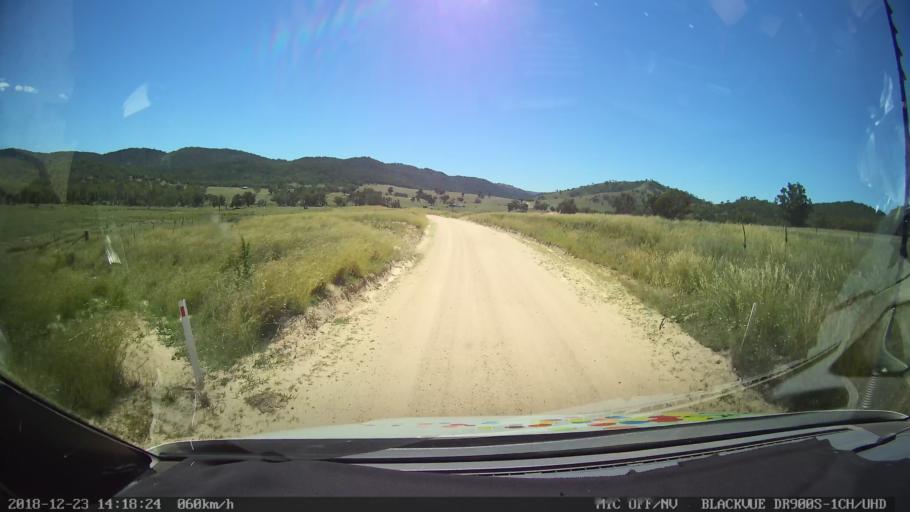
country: AU
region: New South Wales
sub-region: Tamworth Municipality
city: Manilla
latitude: -30.6585
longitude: 151.0039
